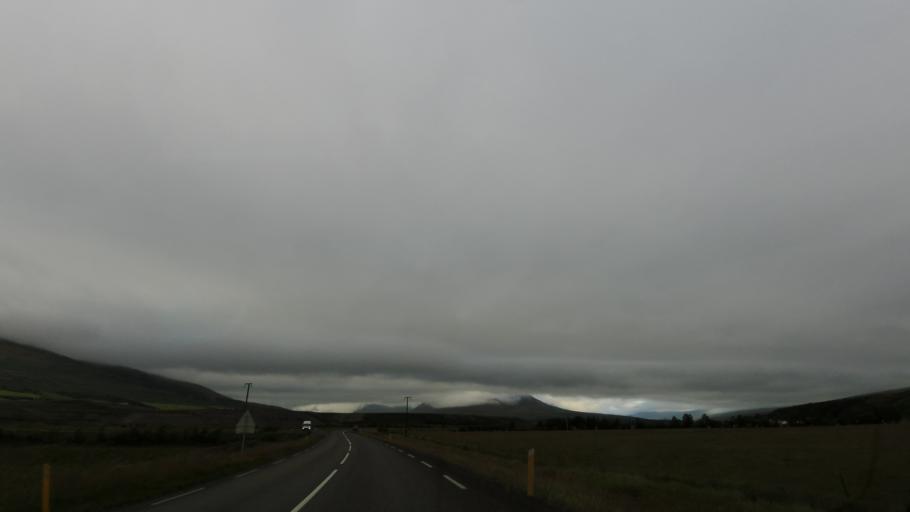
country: IS
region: Northeast
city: Akureyri
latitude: 65.7747
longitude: -17.9165
